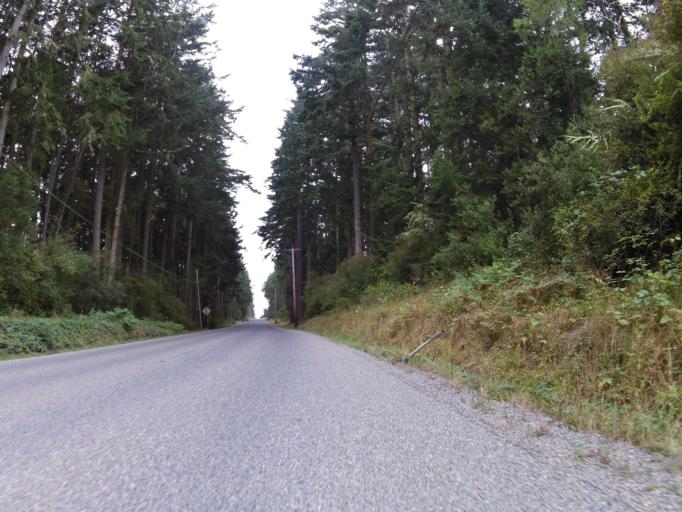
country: US
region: Washington
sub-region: Island County
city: Ault Field
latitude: 48.3007
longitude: -122.6974
